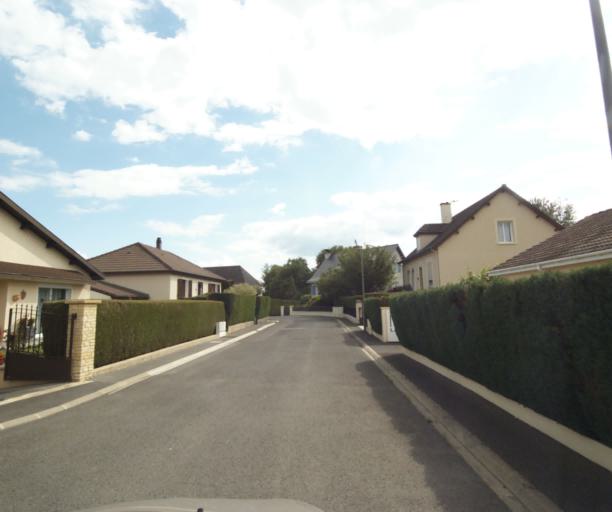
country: FR
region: Champagne-Ardenne
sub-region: Departement des Ardennes
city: Montcy-Notre-Dame
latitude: 49.7580
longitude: 4.7340
